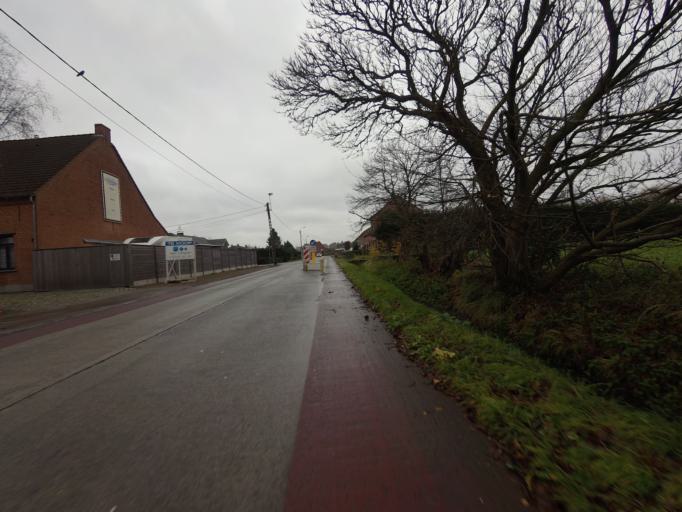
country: BE
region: Flanders
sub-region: Provincie Antwerpen
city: Sint-Katelijne-Waver
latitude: 51.0555
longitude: 4.5264
